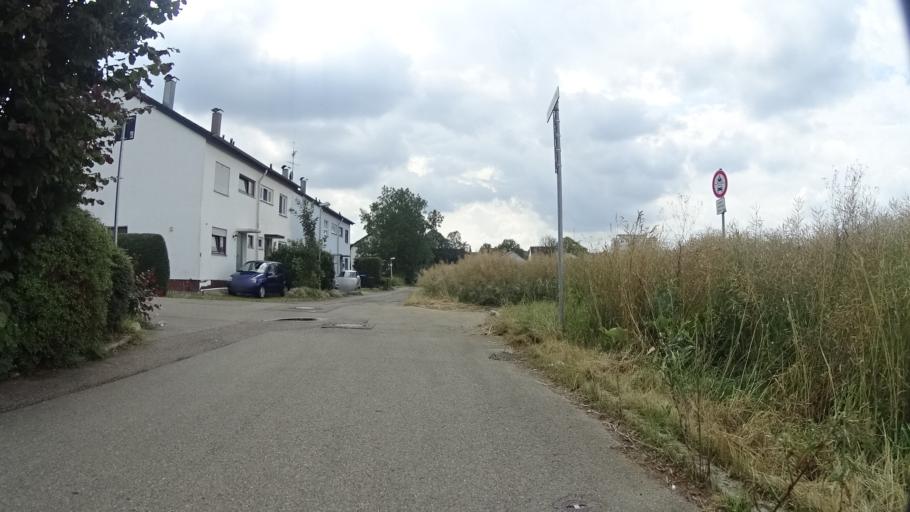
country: DE
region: Baden-Wuerttemberg
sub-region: Regierungsbezirk Stuttgart
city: Eislingen
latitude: 48.6901
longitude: 9.6879
